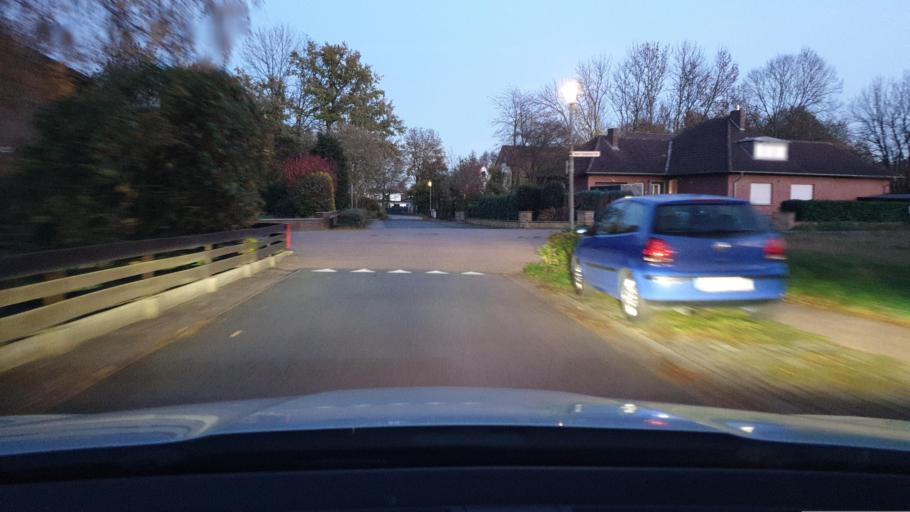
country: DE
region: North Rhine-Westphalia
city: Bad Oeynhausen
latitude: 52.2147
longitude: 8.7824
